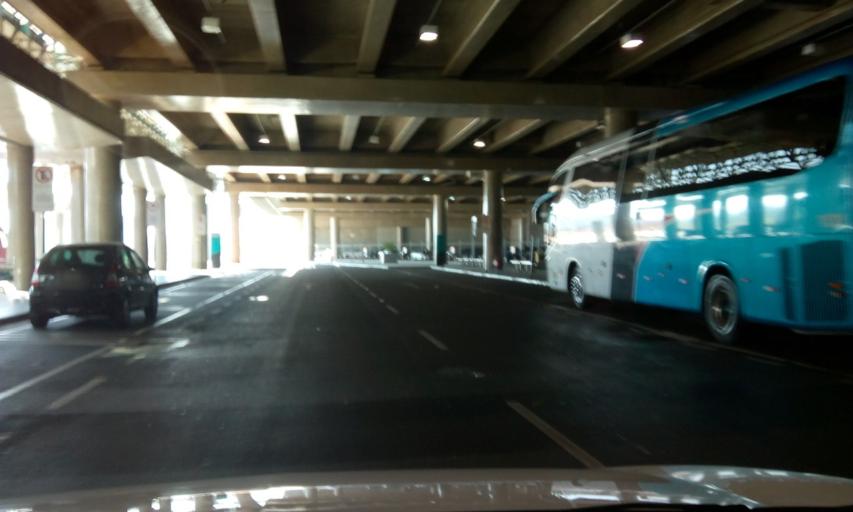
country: BR
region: Sao Paulo
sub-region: Guarulhos
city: Guarulhos
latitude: -23.4234
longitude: -46.4766
